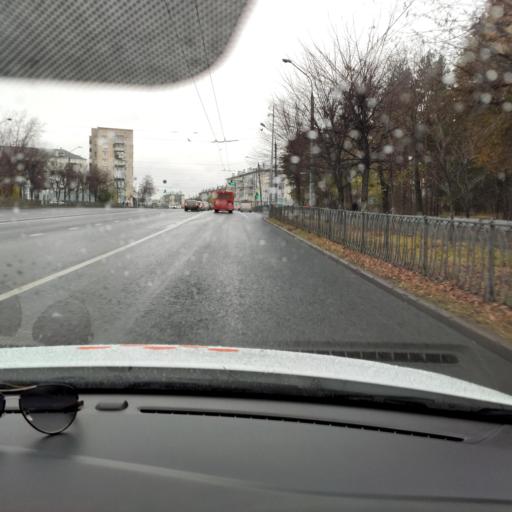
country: RU
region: Tatarstan
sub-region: Gorod Kazan'
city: Kazan
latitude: 55.8243
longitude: 49.0871
